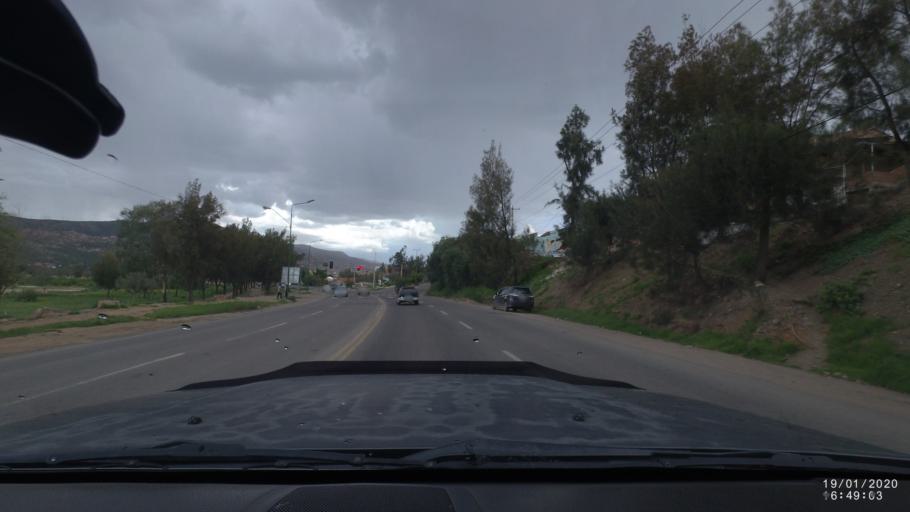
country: BO
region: Cochabamba
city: Cochabamba
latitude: -17.4153
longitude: -66.1418
